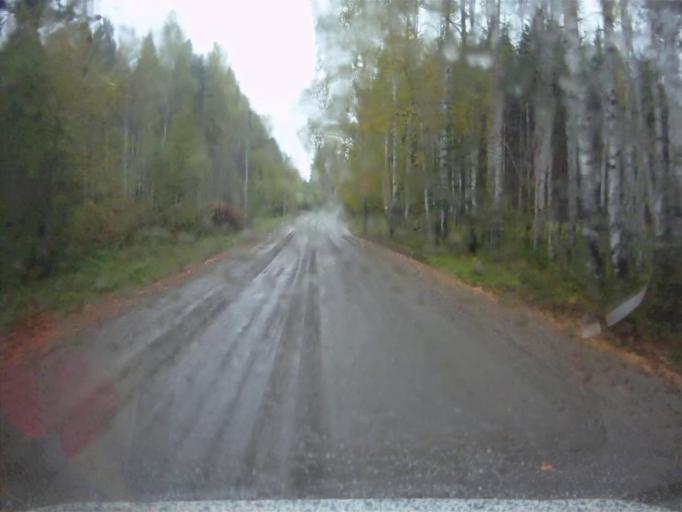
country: RU
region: Chelyabinsk
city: Kyshtym
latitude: 55.8974
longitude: 60.4660
